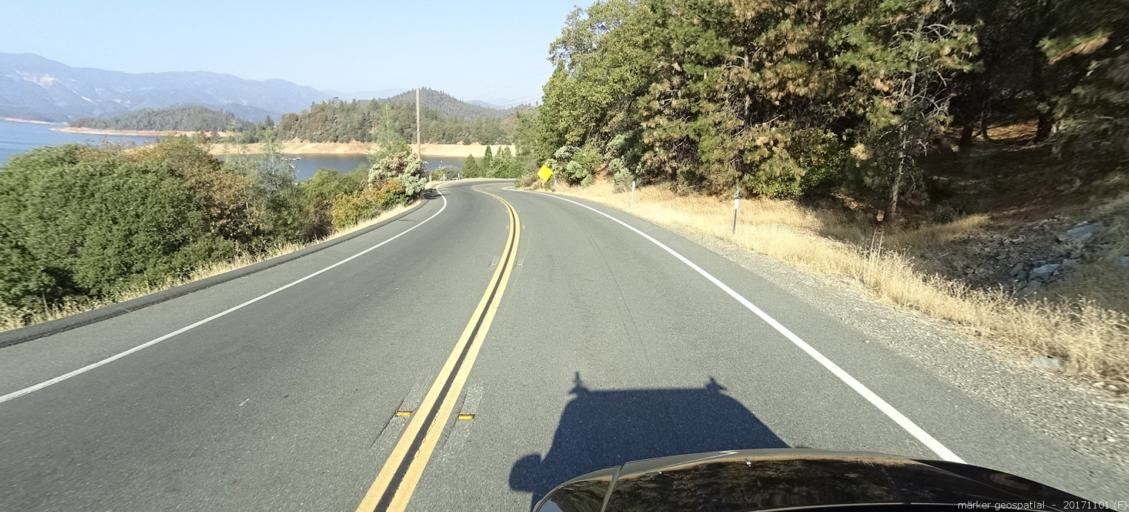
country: US
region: California
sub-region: Shasta County
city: Shasta Lake
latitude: 40.7526
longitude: -122.3221
